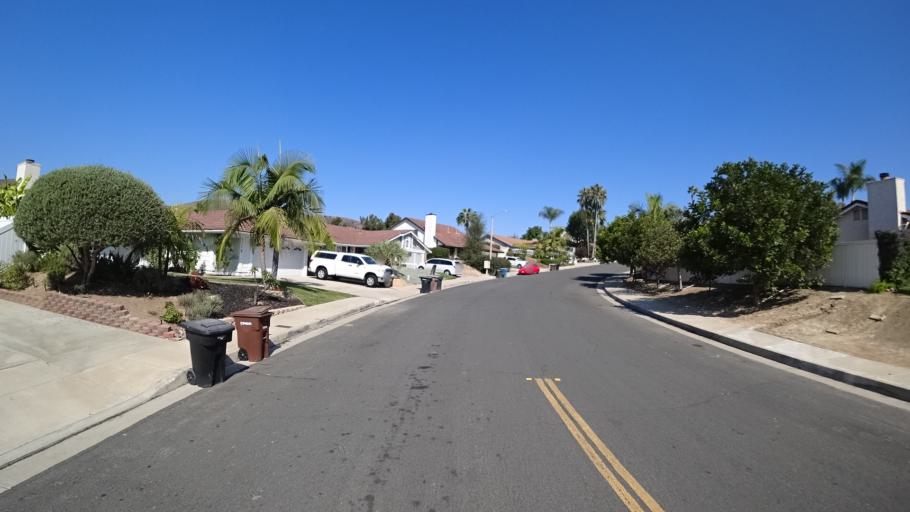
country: US
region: California
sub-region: Orange County
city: San Juan Capistrano
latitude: 33.4710
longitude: -117.6340
